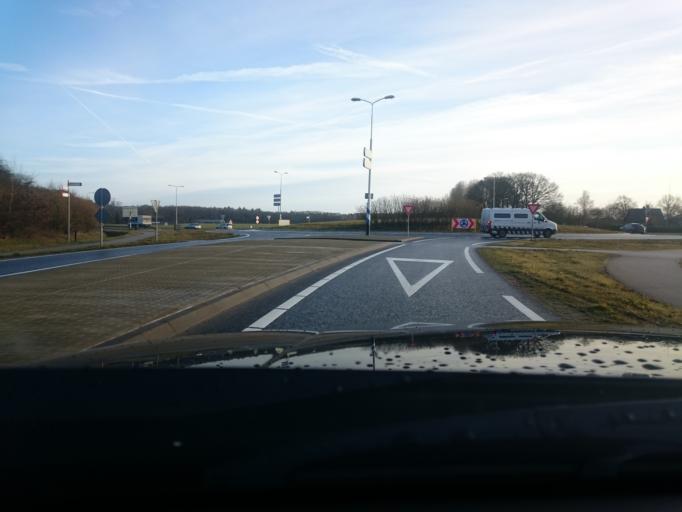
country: NL
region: Overijssel
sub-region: Gemeente Deventer
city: Schalkhaar
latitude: 52.2995
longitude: 6.1977
